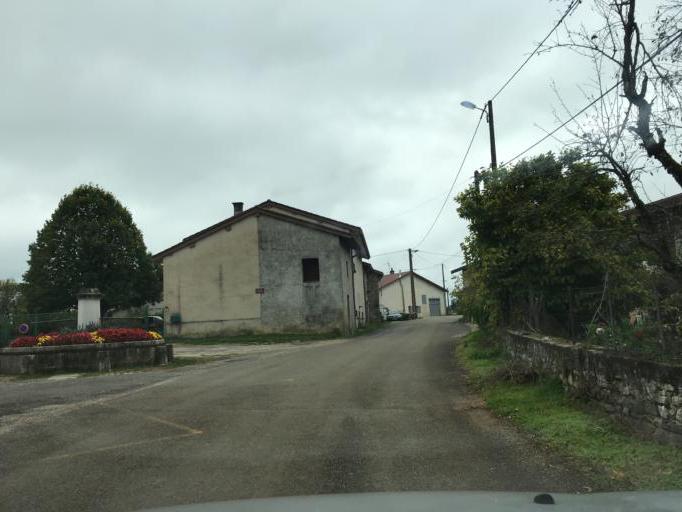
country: FR
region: Franche-Comte
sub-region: Departement du Jura
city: Arinthod
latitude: 46.4316
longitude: 5.4806
